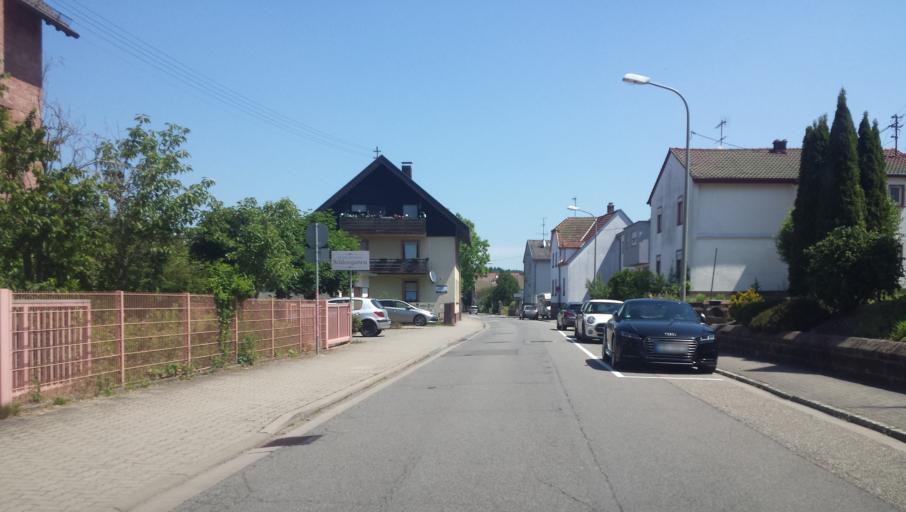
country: DE
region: Rheinland-Pfalz
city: Trippstadt
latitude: 49.3528
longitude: 7.7665
